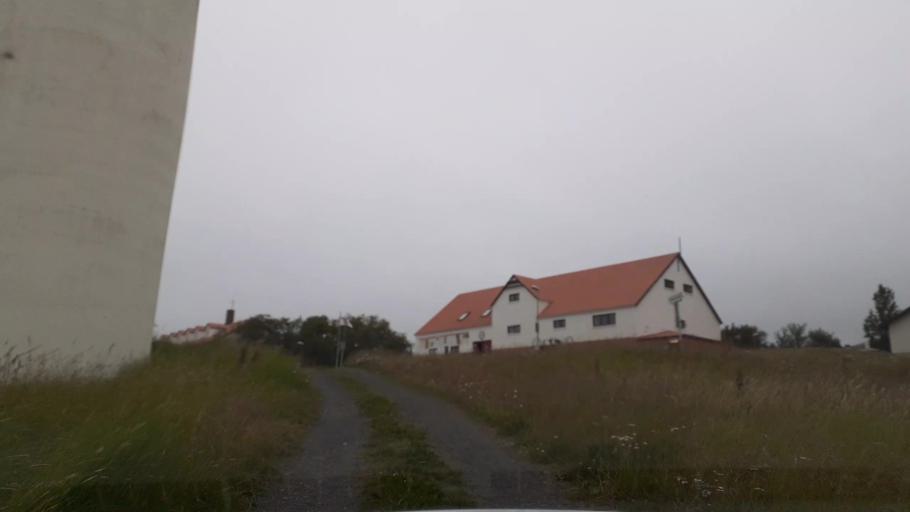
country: IS
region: Northeast
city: Siglufjoerdur
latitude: 65.7323
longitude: -19.1126
